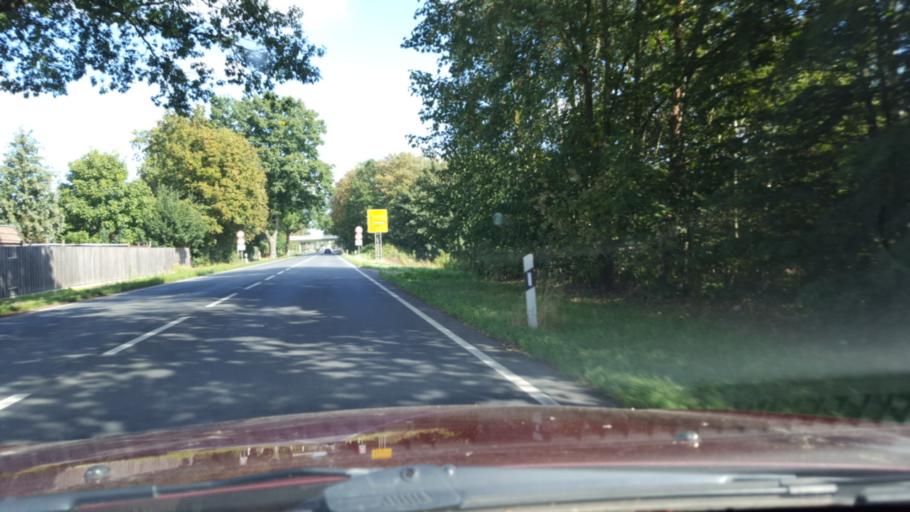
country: DE
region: Lower Saxony
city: Dorverden
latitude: 52.8279
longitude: 9.2074
